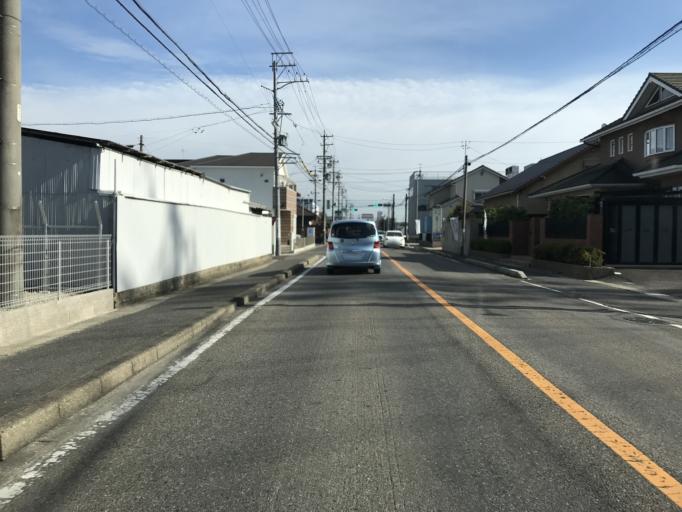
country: JP
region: Aichi
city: Kasugai
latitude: 35.2213
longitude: 136.9417
